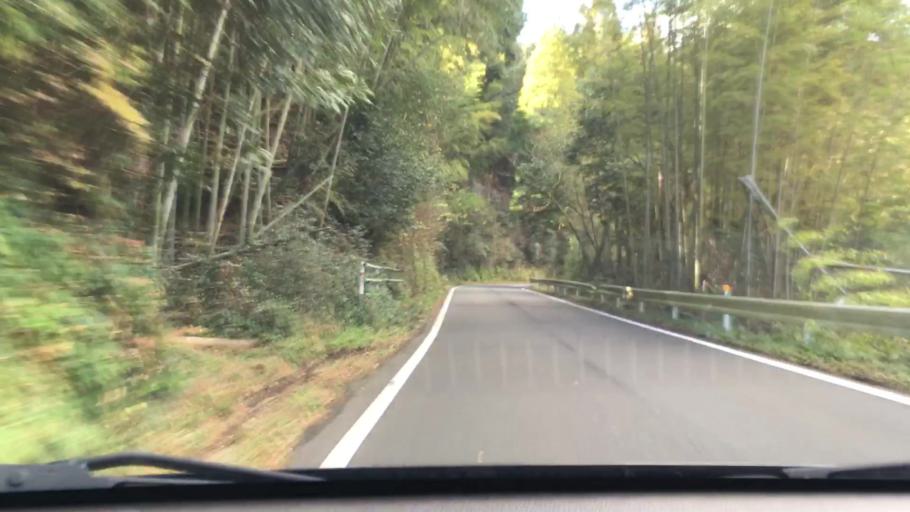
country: JP
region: Kagoshima
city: Ijuin
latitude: 31.7171
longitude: 130.4318
